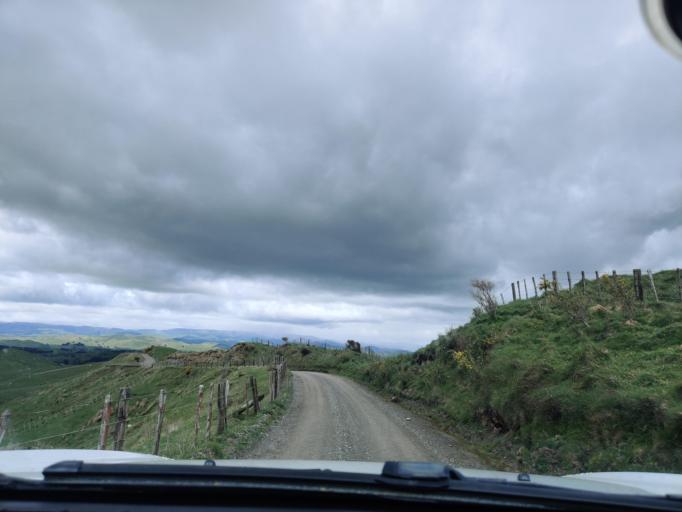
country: NZ
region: Manawatu-Wanganui
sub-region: Palmerston North City
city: Palmerston North
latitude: -40.2839
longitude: 175.8599
